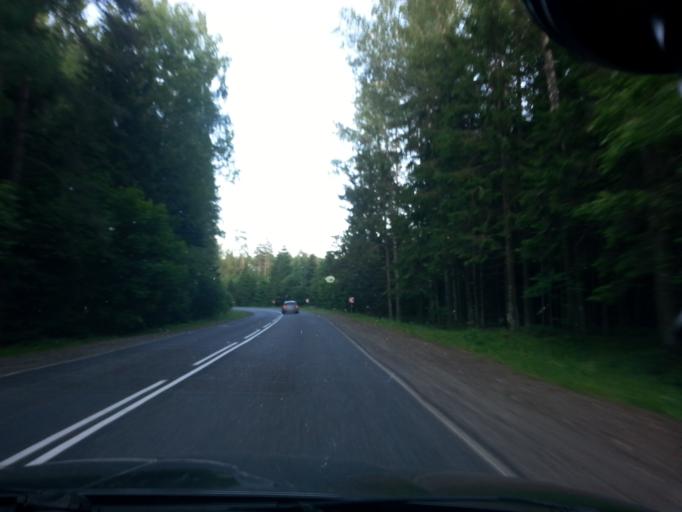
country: BY
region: Minsk
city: Svir
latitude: 54.9246
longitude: 26.5348
